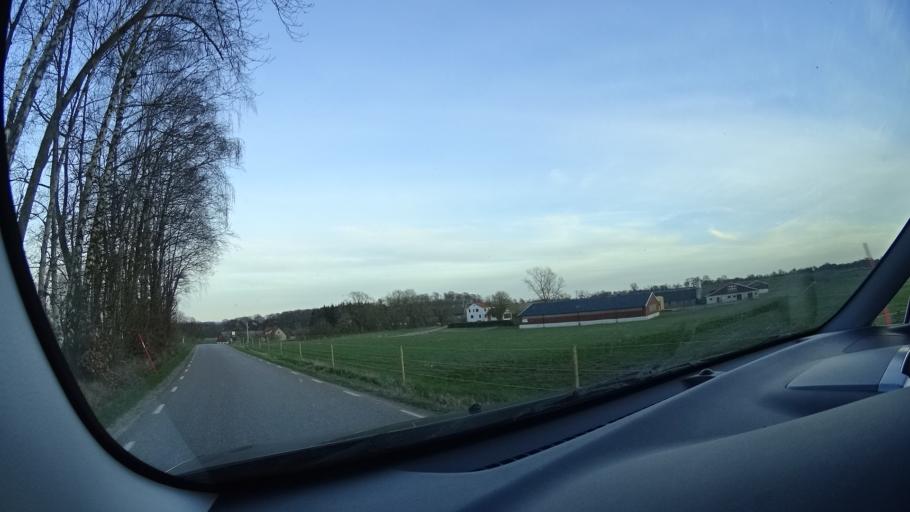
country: SE
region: Skane
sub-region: Eslovs Kommun
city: Stehag
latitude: 55.8889
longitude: 13.4259
